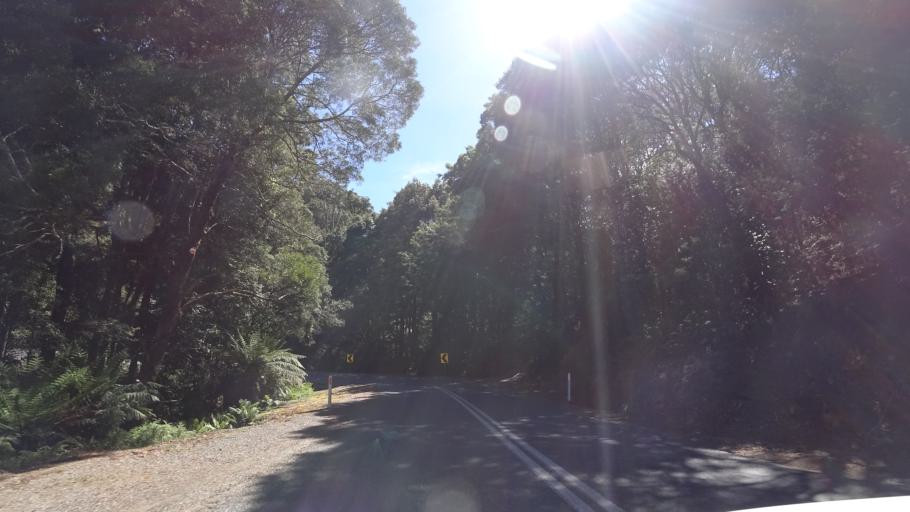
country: AU
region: Tasmania
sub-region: Break O'Day
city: St Helens
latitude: -41.2224
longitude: 147.9546
